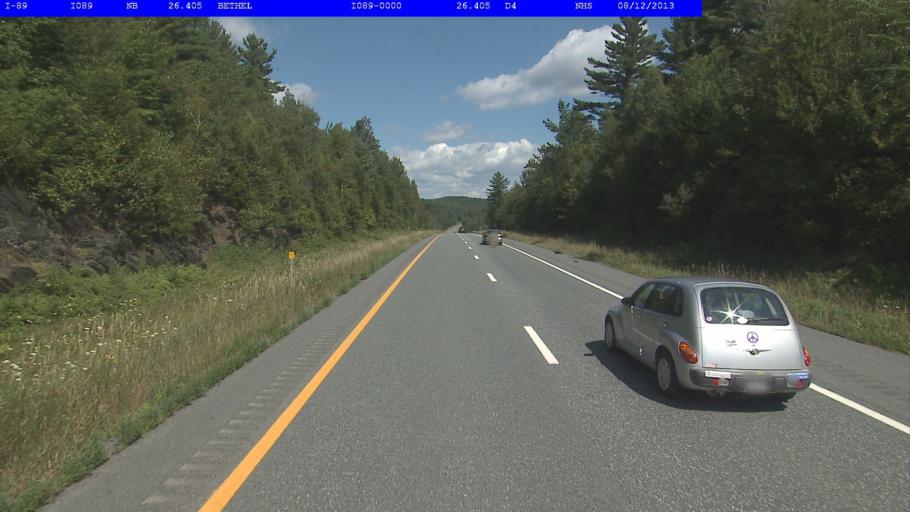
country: US
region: Vermont
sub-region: Orange County
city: Randolph
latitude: 43.8807
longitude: -72.6152
